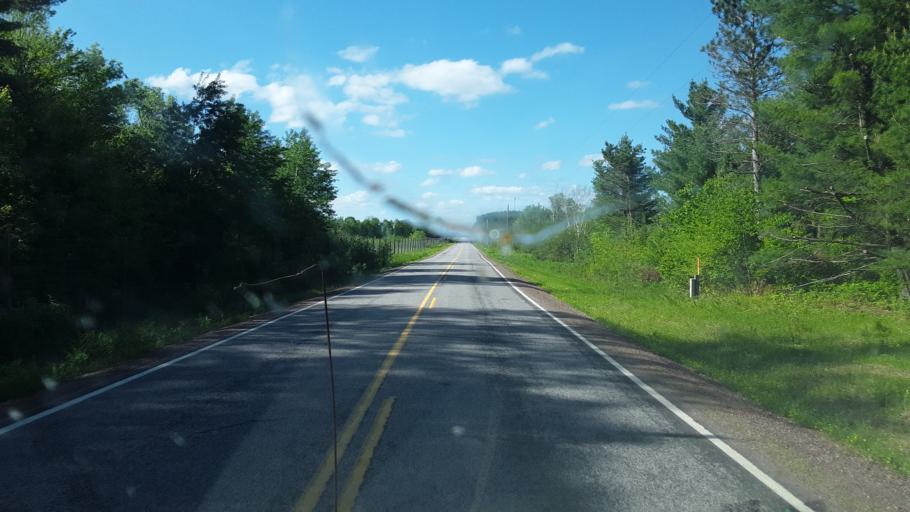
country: US
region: Wisconsin
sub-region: Wood County
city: Nekoosa
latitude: 44.3233
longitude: -90.1308
